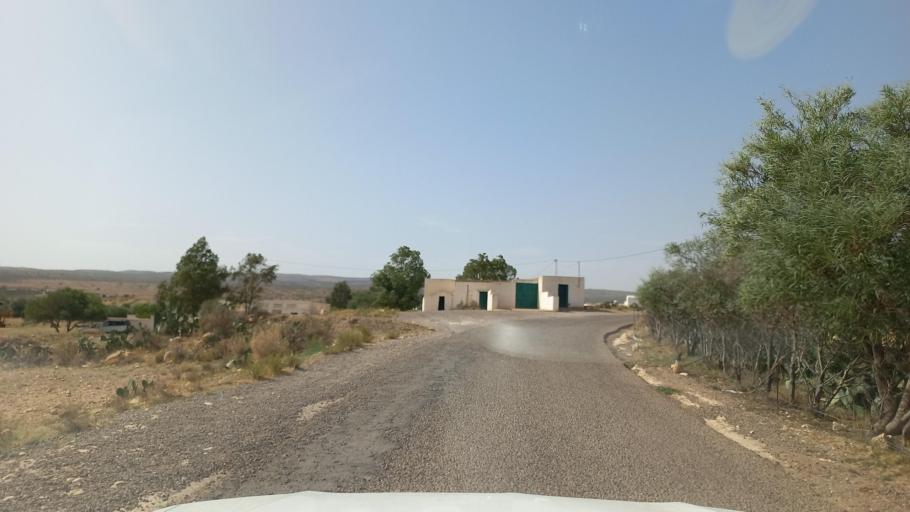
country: TN
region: Al Qasrayn
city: Kasserine
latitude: 35.3011
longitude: 8.9508
